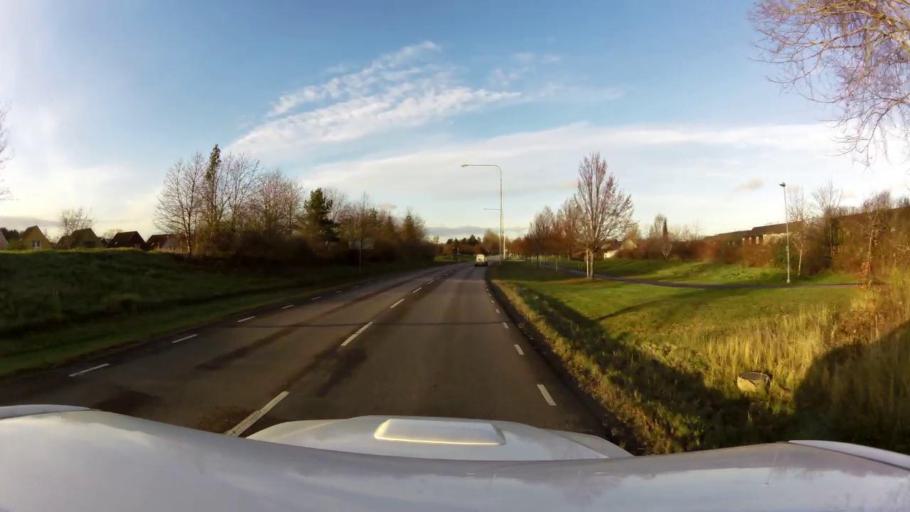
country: SE
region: OEstergoetland
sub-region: Linkopings Kommun
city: Linkoping
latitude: 58.3763
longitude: 15.6622
